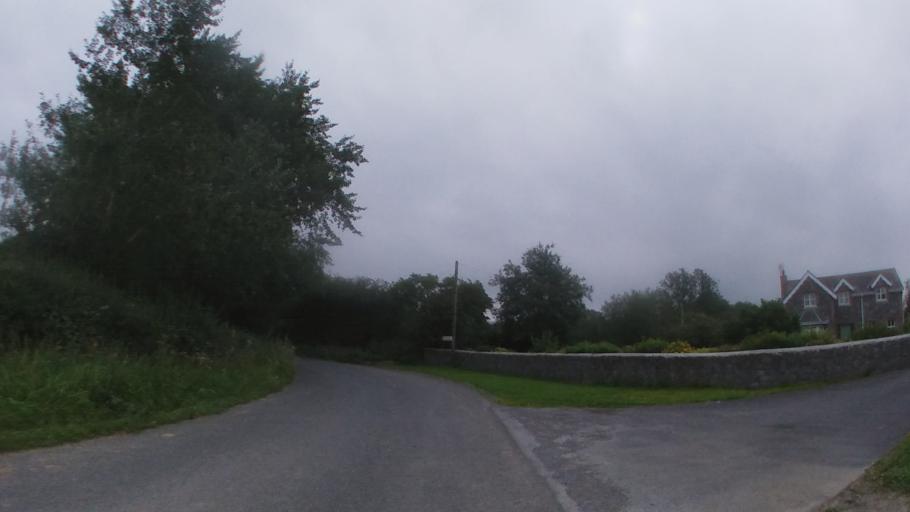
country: IE
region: Leinster
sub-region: Kilkenny
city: Kilkenny
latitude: 52.6983
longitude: -7.1944
